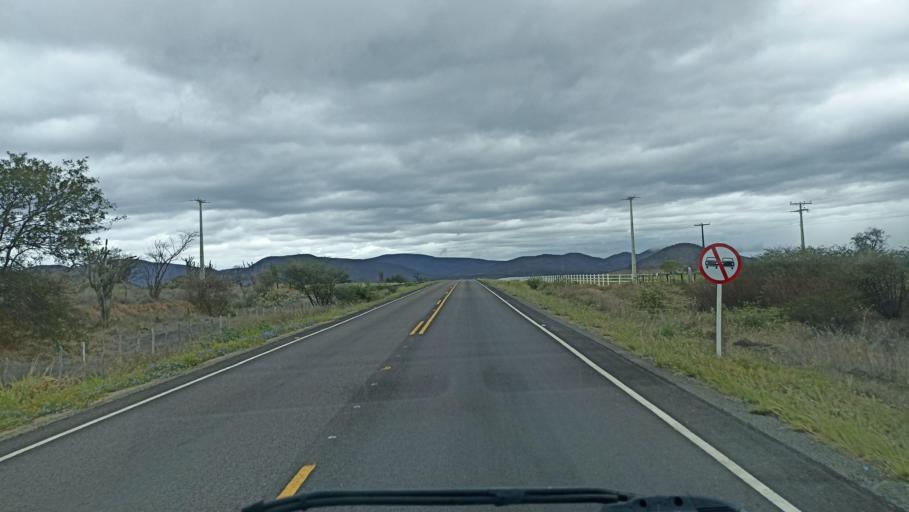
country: BR
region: Bahia
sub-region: Iacu
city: Iacu
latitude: -12.9146
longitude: -40.4108
